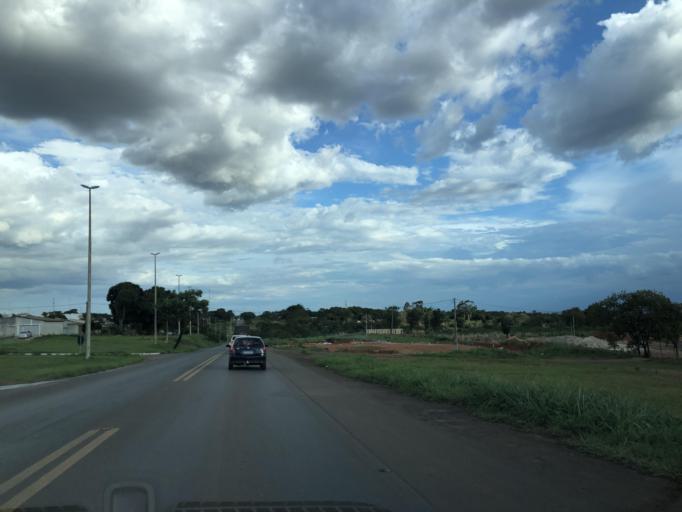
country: BR
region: Goias
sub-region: Luziania
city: Luziania
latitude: -16.0362
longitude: -48.0699
